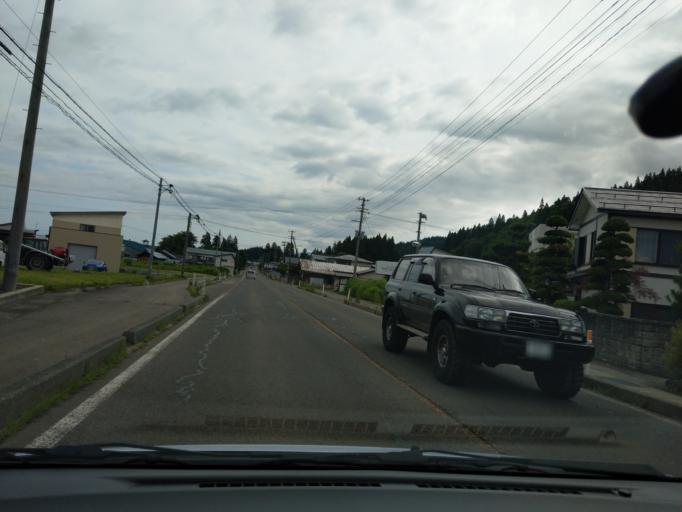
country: JP
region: Akita
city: Yokotemachi
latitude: 39.3645
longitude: 140.5661
